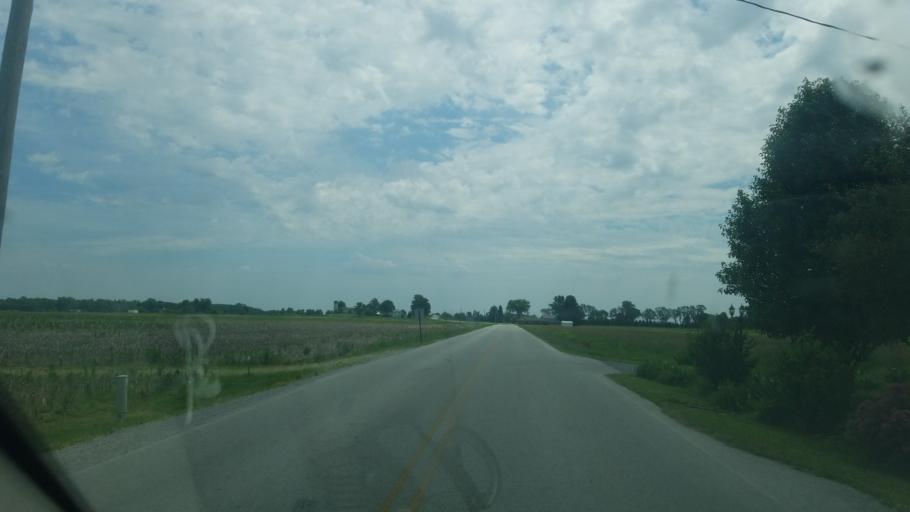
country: US
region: Ohio
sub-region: Wood County
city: Bowling Green
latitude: 41.2975
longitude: -83.6444
